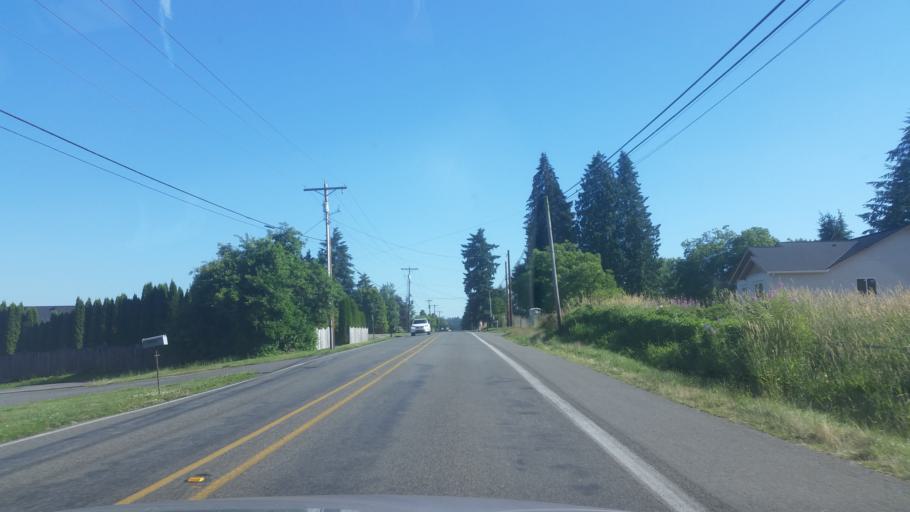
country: US
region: Washington
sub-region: Snohomish County
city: Cathcart
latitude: 47.8625
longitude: -122.0991
